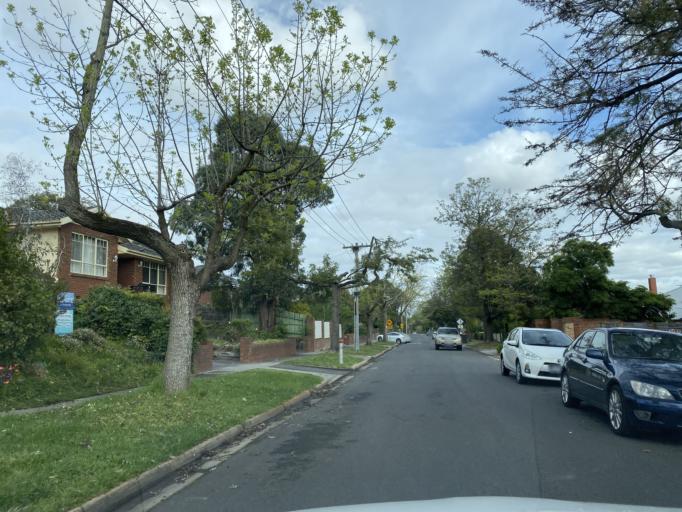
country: AU
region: Victoria
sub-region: Boroondara
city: Ashburton
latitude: -37.8450
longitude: 145.0913
